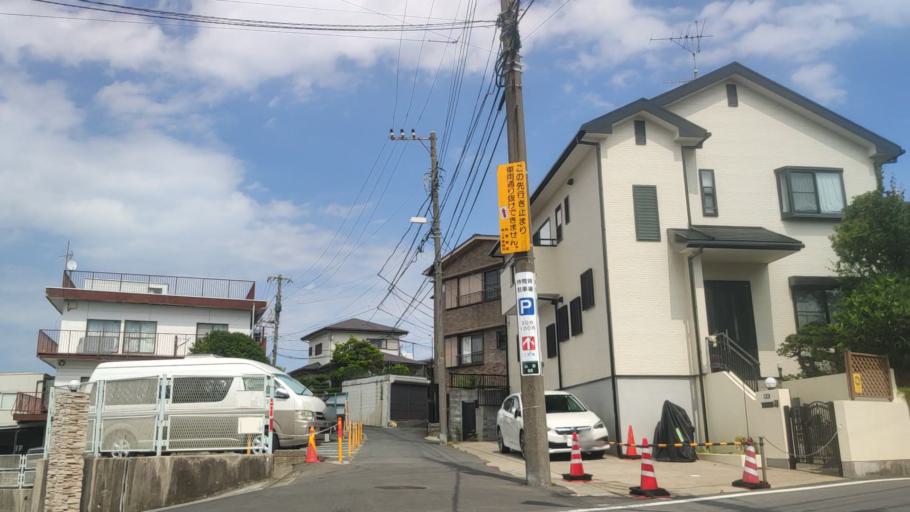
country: JP
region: Kanagawa
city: Yokohama
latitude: 35.4299
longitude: 139.6258
